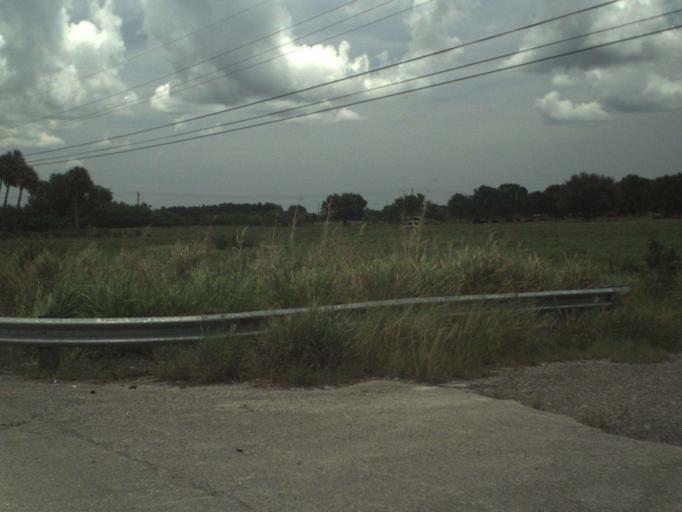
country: US
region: Florida
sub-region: Saint Lucie County
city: Lakewood Park
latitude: 27.4603
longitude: -80.3990
